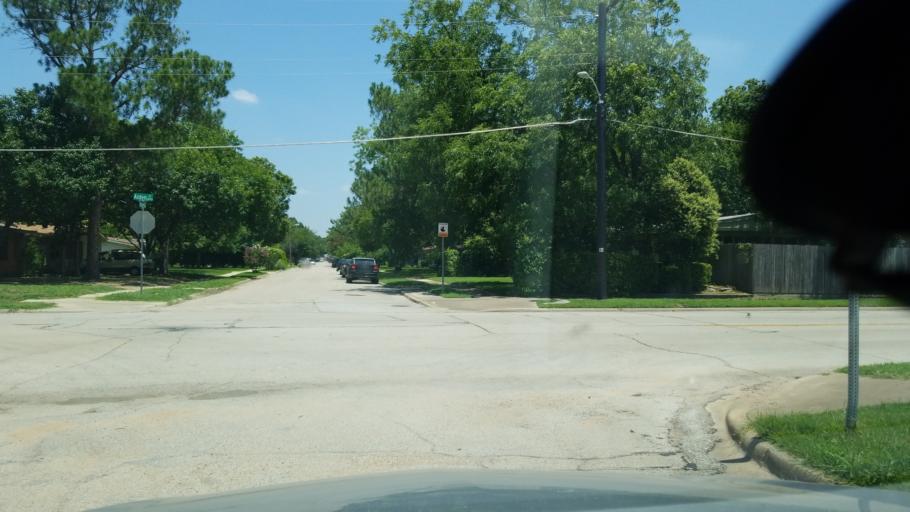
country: US
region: Texas
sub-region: Dallas County
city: Irving
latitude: 32.8280
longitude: -96.9700
